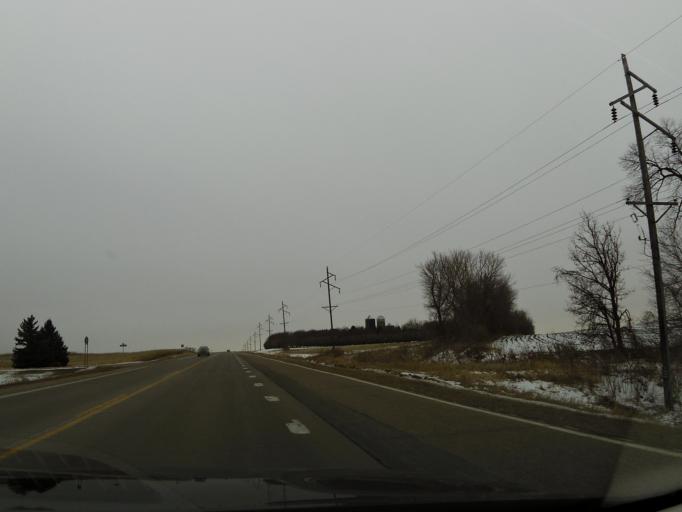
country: US
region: Minnesota
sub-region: Scott County
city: Jordan
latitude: 44.6385
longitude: -93.6187
